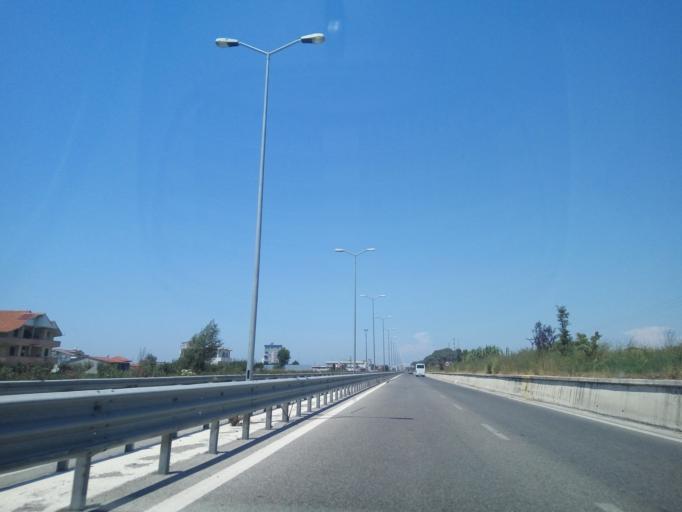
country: AL
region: Tirane
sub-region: Rrethi i Kavajes
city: Golem
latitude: 41.2173
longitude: 19.5302
